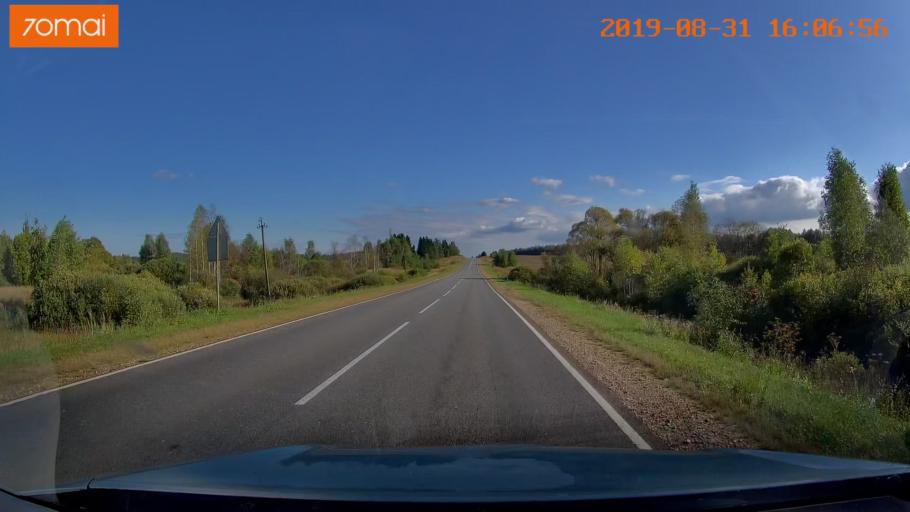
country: RU
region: Kaluga
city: Yukhnov
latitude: 54.6176
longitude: 35.3518
